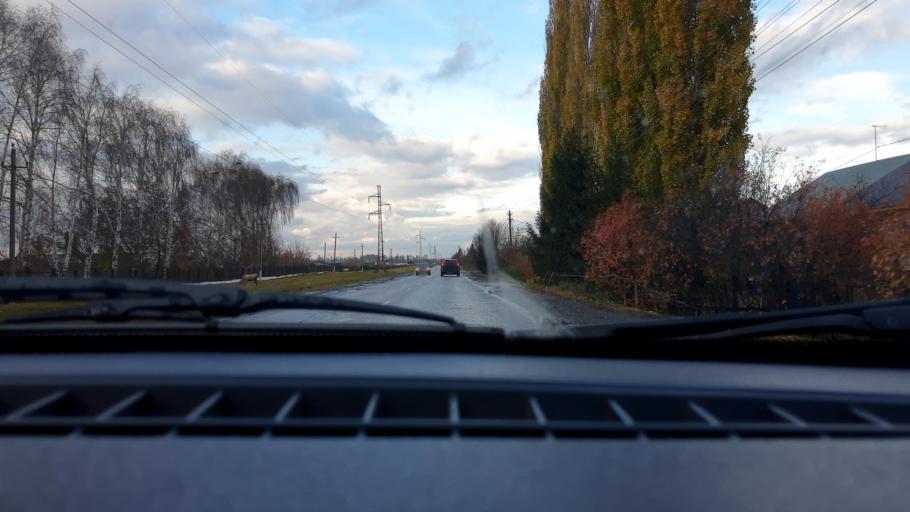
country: RU
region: Bashkortostan
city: Ufa
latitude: 54.8355
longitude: 55.9964
